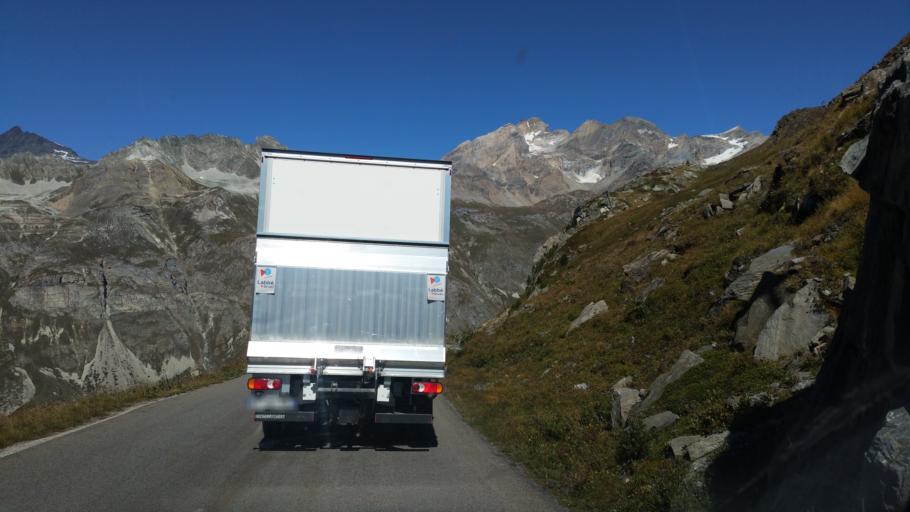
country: FR
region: Rhone-Alpes
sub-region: Departement de la Savoie
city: Val-d'Isere
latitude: 45.4359
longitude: 7.0027
